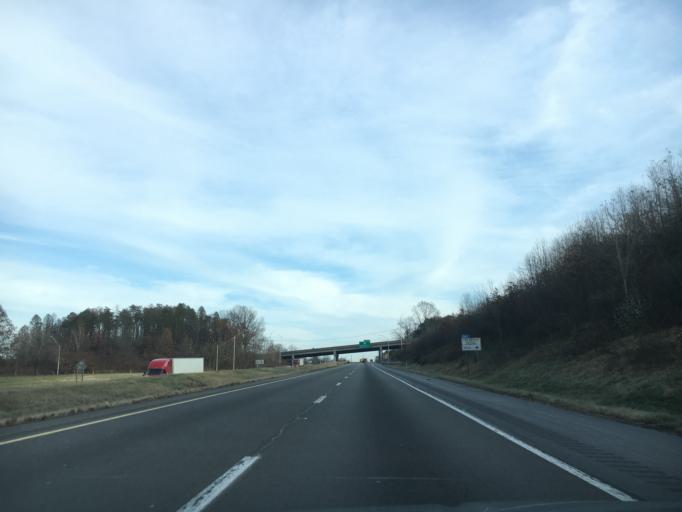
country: US
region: Pennsylvania
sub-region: Columbia County
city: Light Street
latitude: 41.0274
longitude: -76.4293
